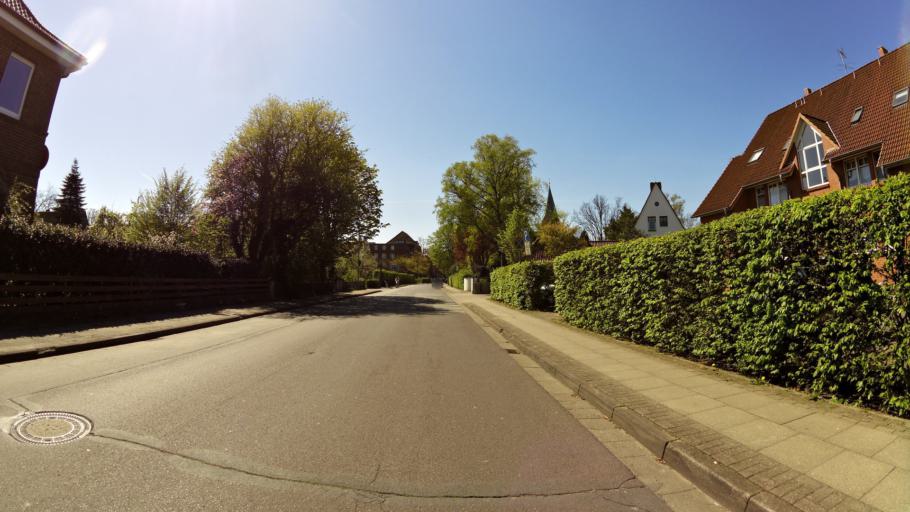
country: DE
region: Lower Saxony
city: Rotenburg
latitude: 53.1081
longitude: 9.4131
